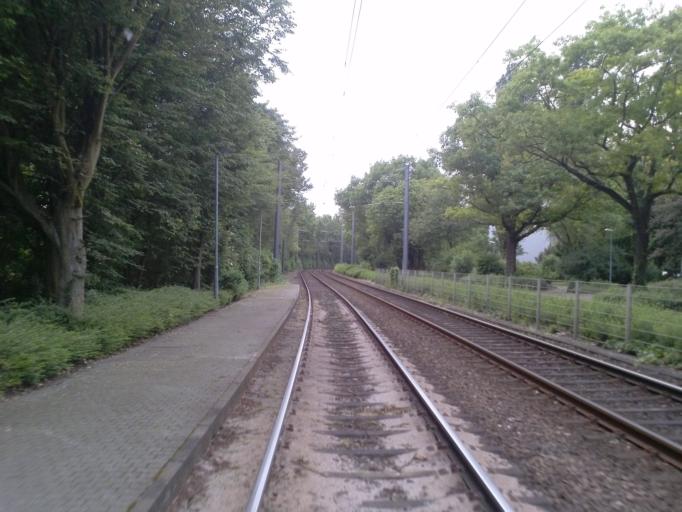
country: DE
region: Baden-Wuerttemberg
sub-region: Karlsruhe Region
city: Karlsruhe
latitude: 49.0081
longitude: 8.3632
